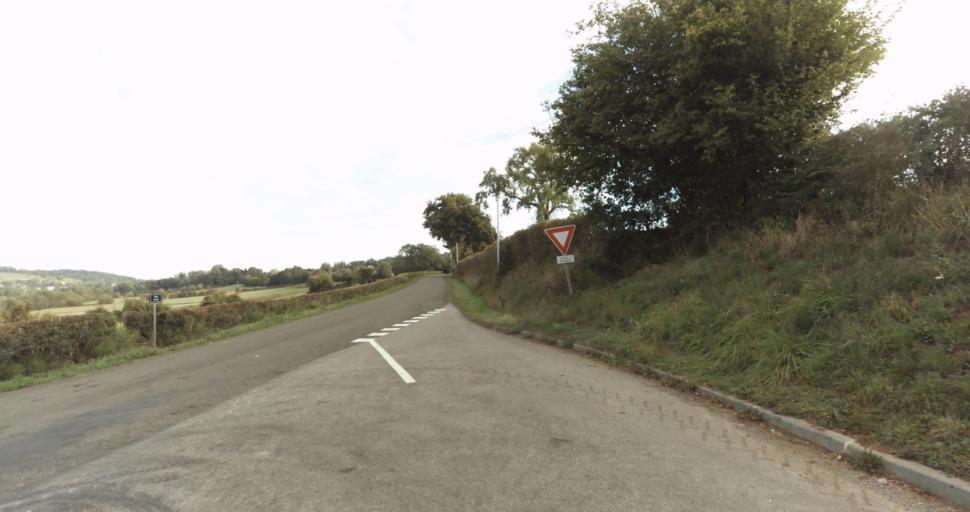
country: FR
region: Lower Normandy
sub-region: Departement de l'Orne
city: Vimoutiers
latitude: 48.9052
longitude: 0.2154
